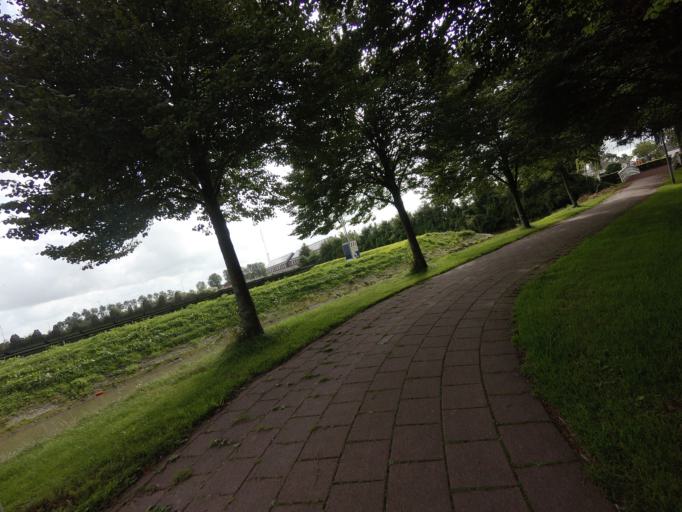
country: NL
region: North Holland
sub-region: Gemeente Medemblik
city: Opperdoes
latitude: 52.7240
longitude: 5.0776
